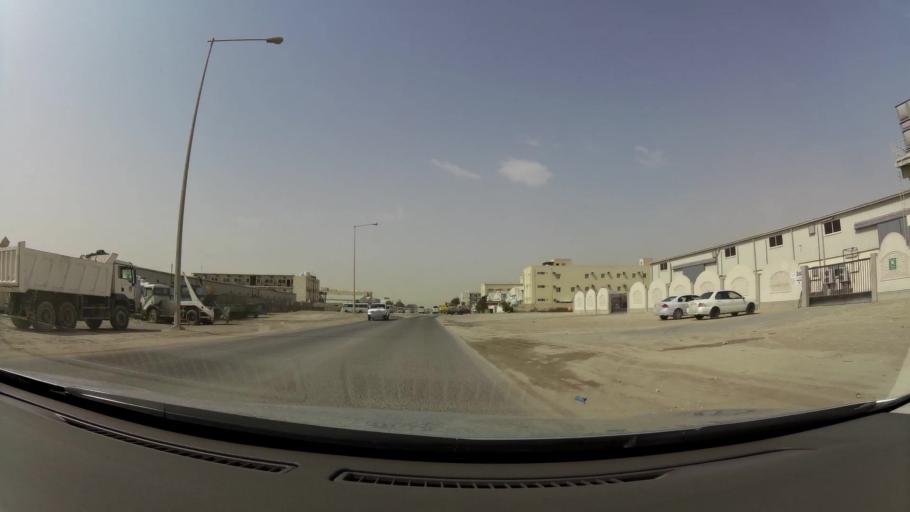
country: QA
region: Al Wakrah
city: Al Wukayr
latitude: 25.1716
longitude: 51.4673
